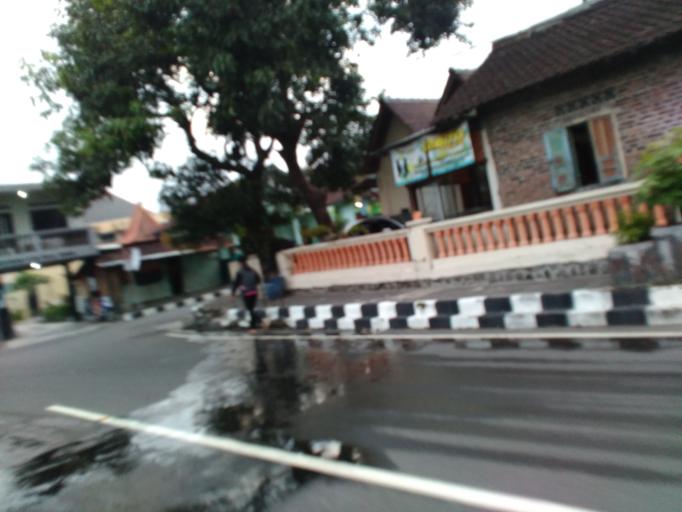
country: ID
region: Central Java
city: Boyolali
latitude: -7.5341
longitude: 110.6025
